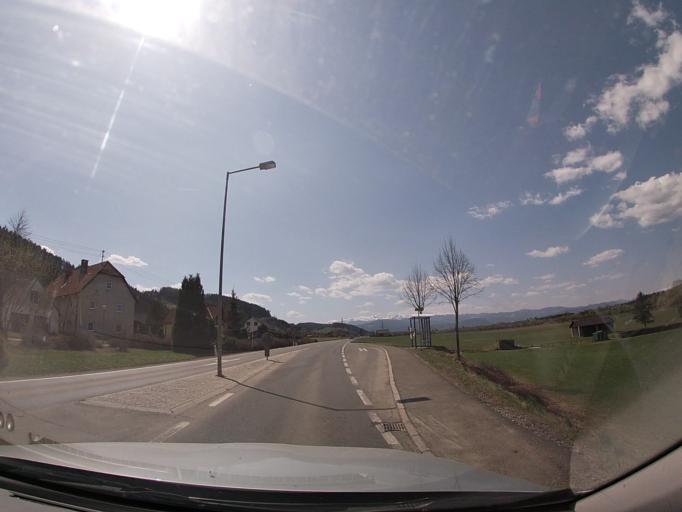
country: AT
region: Styria
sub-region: Politischer Bezirk Murtal
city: Apfelberg
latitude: 47.1929
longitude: 14.8262
